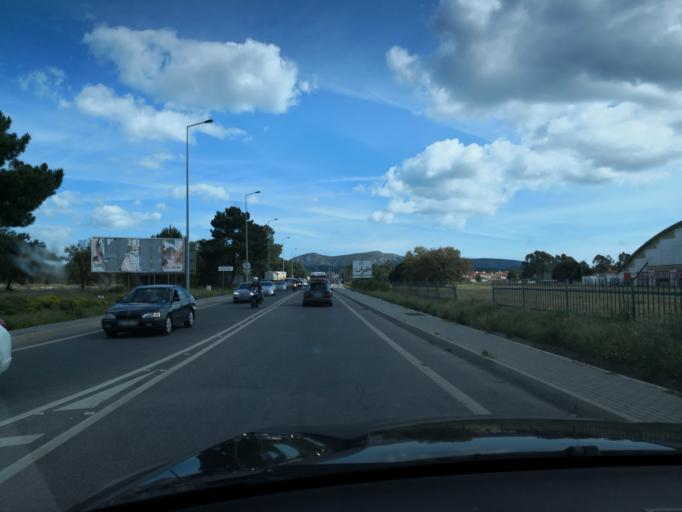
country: PT
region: Setubal
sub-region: Palmela
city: Quinta do Anjo
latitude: 38.5347
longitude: -9.0233
